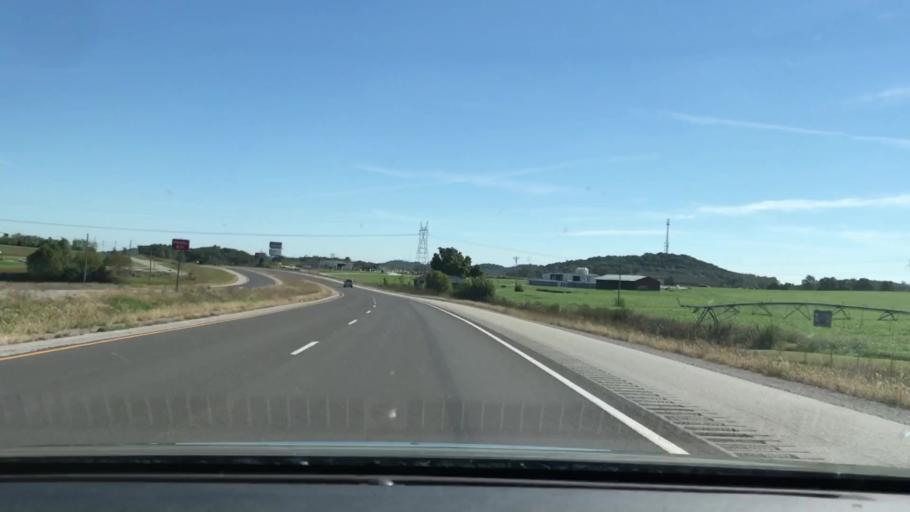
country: US
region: Kentucky
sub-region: Logan County
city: Russellville
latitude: 36.8356
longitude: -86.9326
